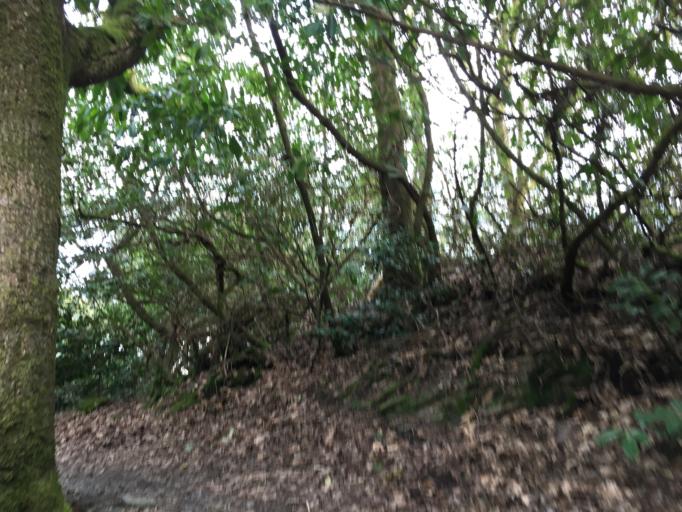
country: GB
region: Wales
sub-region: Gwynedd
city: Porthmadog
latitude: 52.9111
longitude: -4.1004
